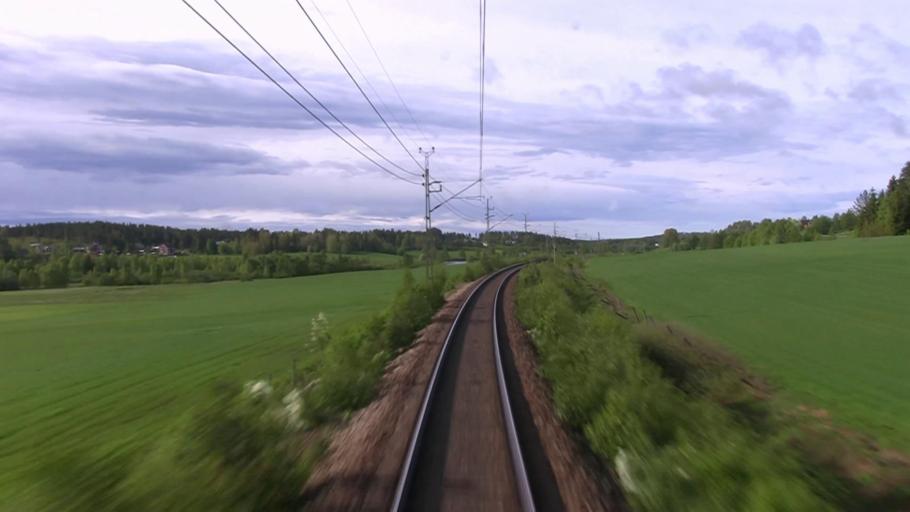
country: SE
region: Vaesterbotten
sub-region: Vindelns Kommun
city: Vindeln
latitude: 64.1060
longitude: 19.6842
